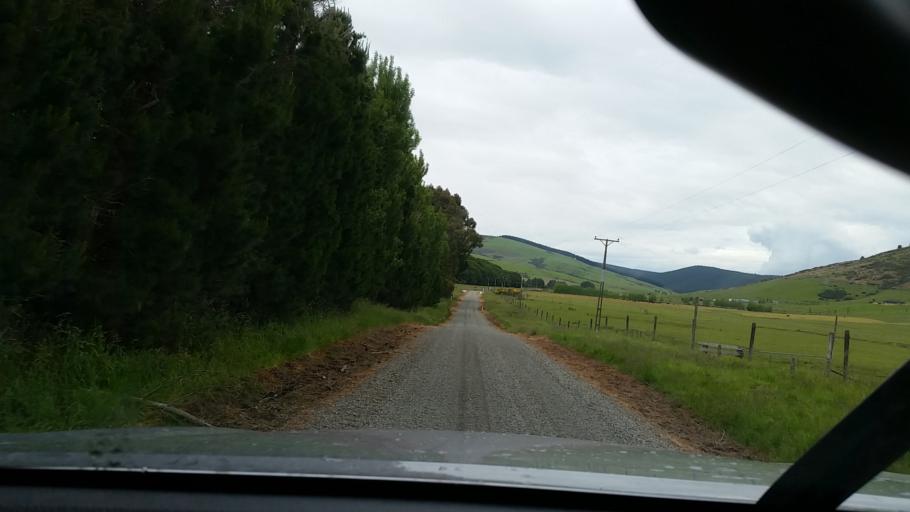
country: NZ
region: Southland
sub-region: Southland District
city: Winton
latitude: -45.9440
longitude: 168.1600
